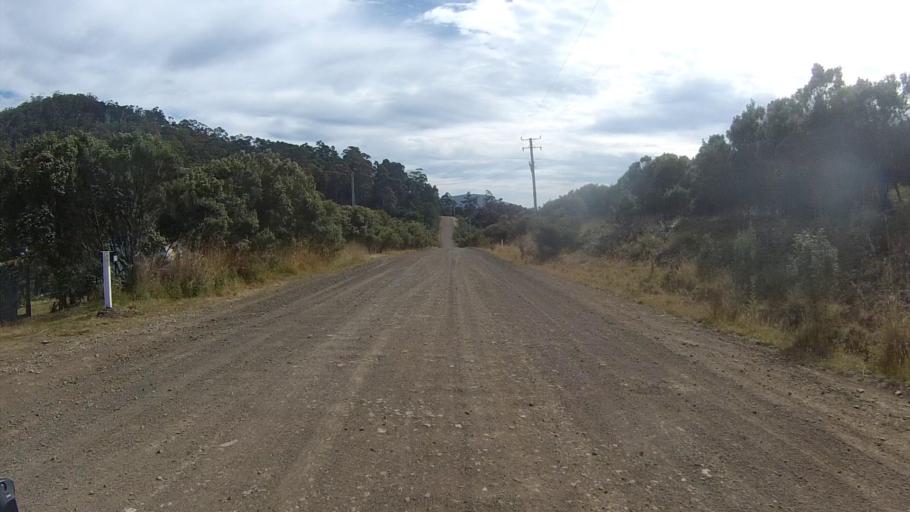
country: AU
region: Tasmania
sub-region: Sorell
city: Sorell
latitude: -42.7769
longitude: 147.8267
